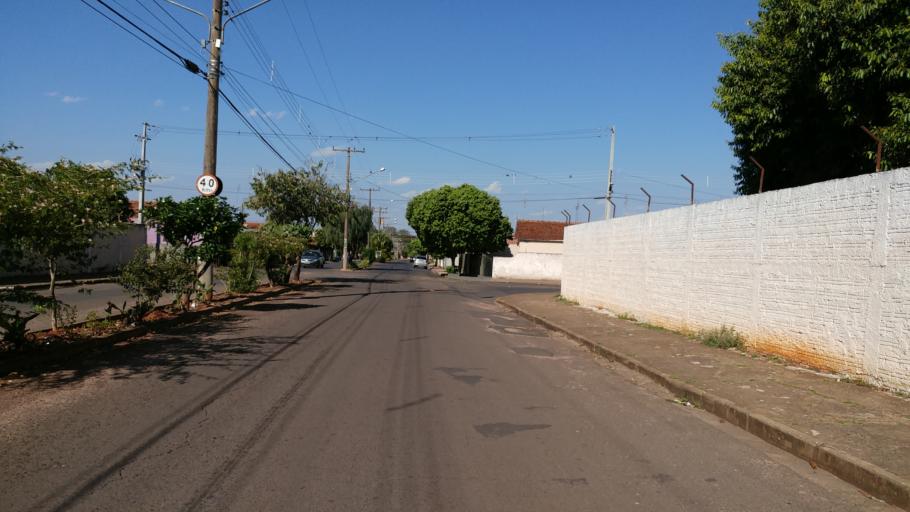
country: BR
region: Sao Paulo
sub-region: Paraguacu Paulista
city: Paraguacu Paulista
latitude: -22.4272
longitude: -50.5760
